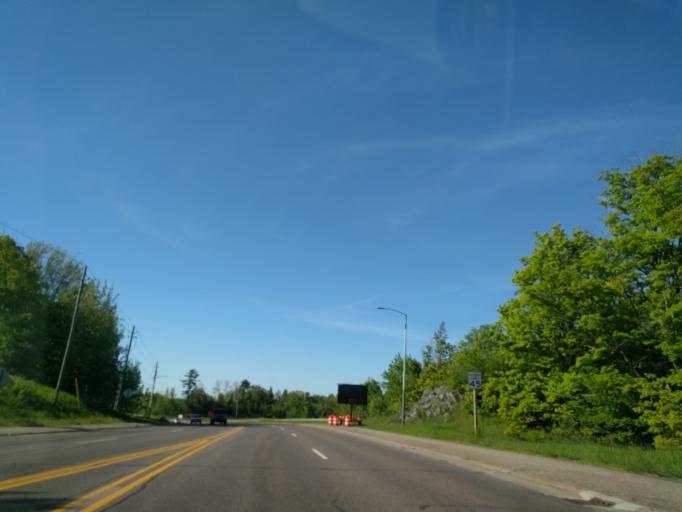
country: US
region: Michigan
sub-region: Marquette County
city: Marquette
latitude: 46.5369
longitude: -87.4171
